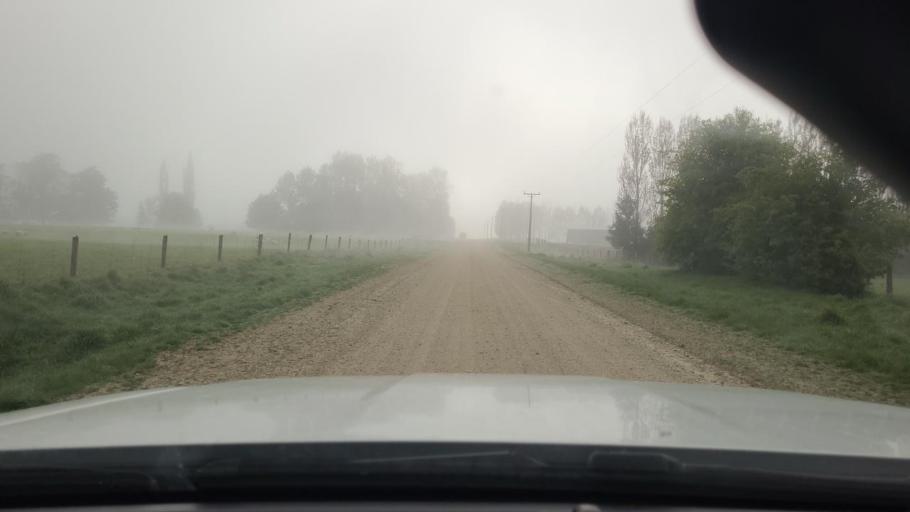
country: NZ
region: Otago
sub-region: Queenstown-Lakes District
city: Kingston
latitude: -45.6004
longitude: 168.9756
